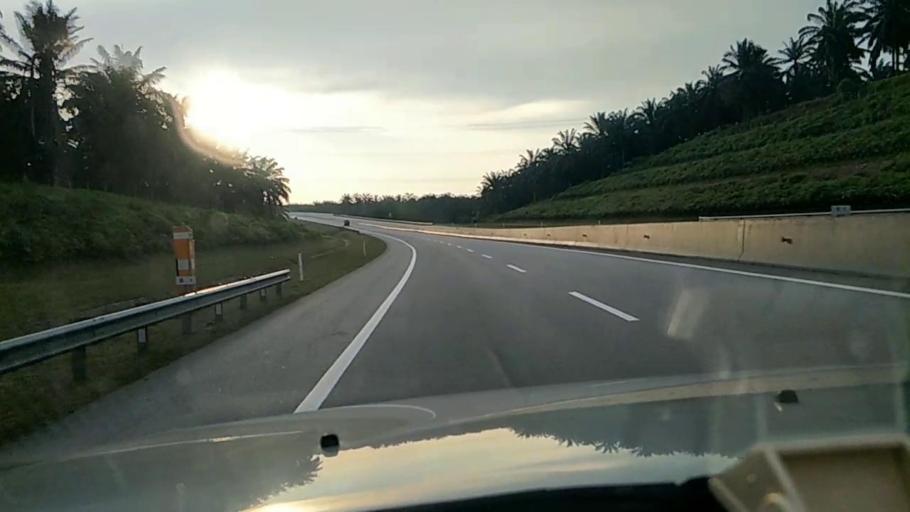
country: MY
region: Selangor
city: Batu Arang
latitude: 3.2873
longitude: 101.4378
